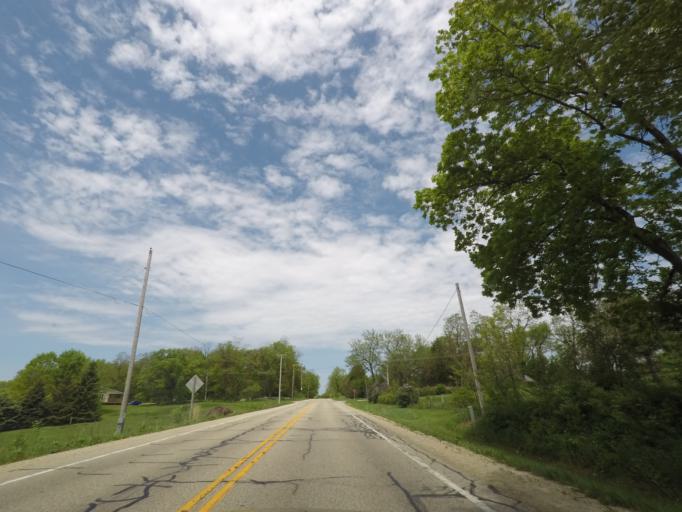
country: US
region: Wisconsin
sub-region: Rock County
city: Orfordville
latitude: 42.6432
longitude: -89.2796
